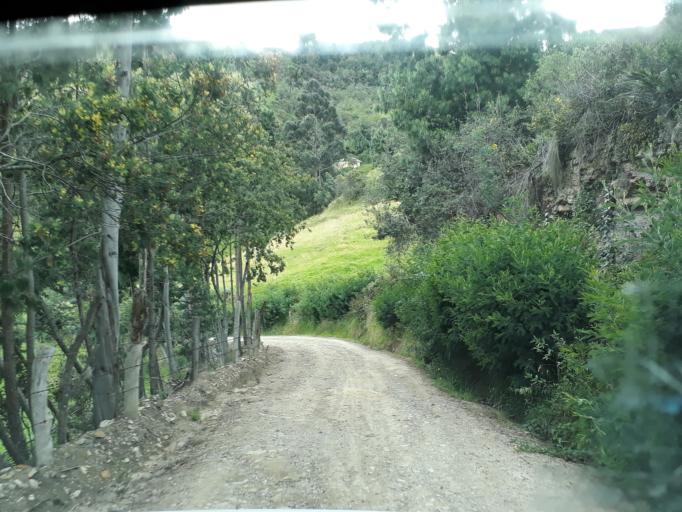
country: CO
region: Cundinamarca
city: La Mesa
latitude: 5.2676
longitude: -73.9005
